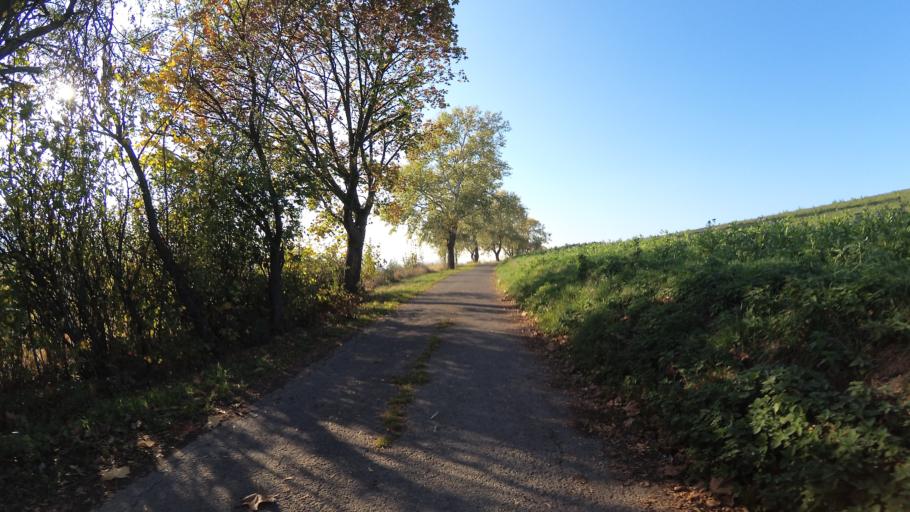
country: DE
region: Saarland
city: Sankt Wendel
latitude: 49.4562
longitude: 7.1915
